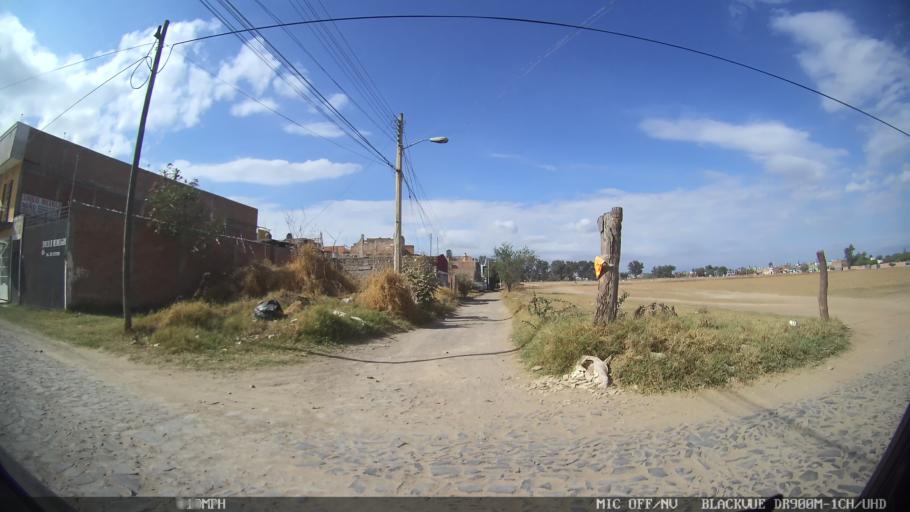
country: MX
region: Jalisco
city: Tonala
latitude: 20.6535
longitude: -103.2441
